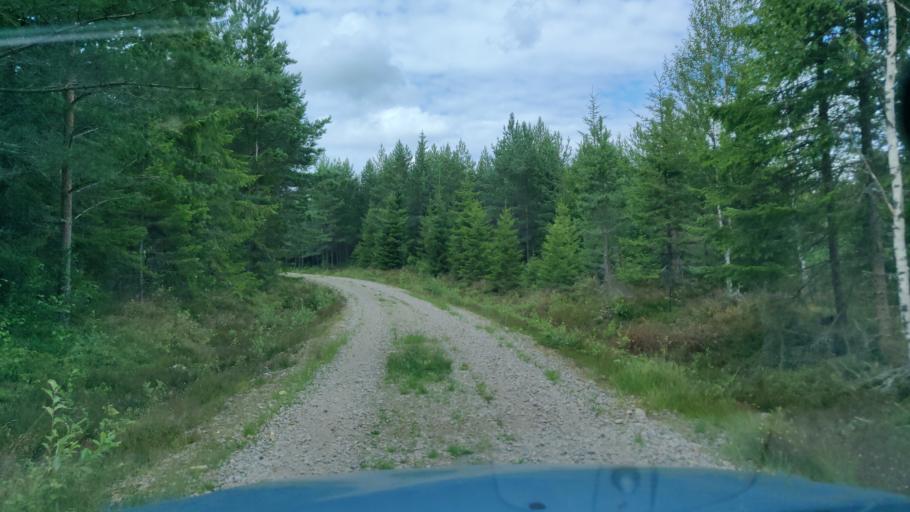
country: SE
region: Vaermland
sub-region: Hagfors Kommun
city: Hagfors
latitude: 59.9643
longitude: 13.5864
